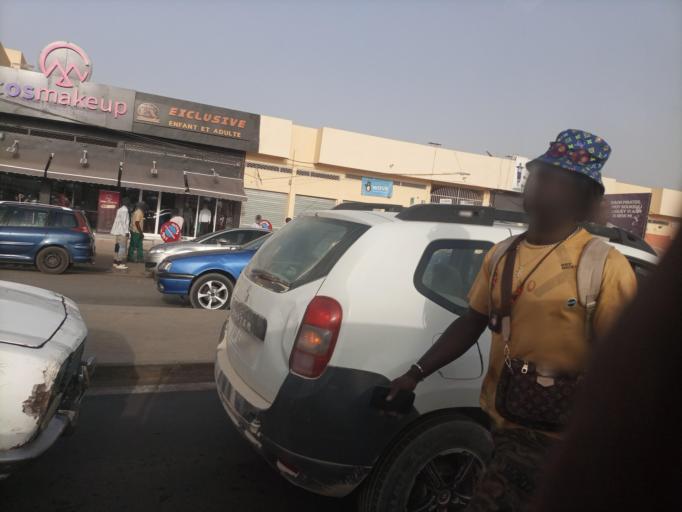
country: SN
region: Thies
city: Nguekhokh
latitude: 14.4456
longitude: -16.9806
